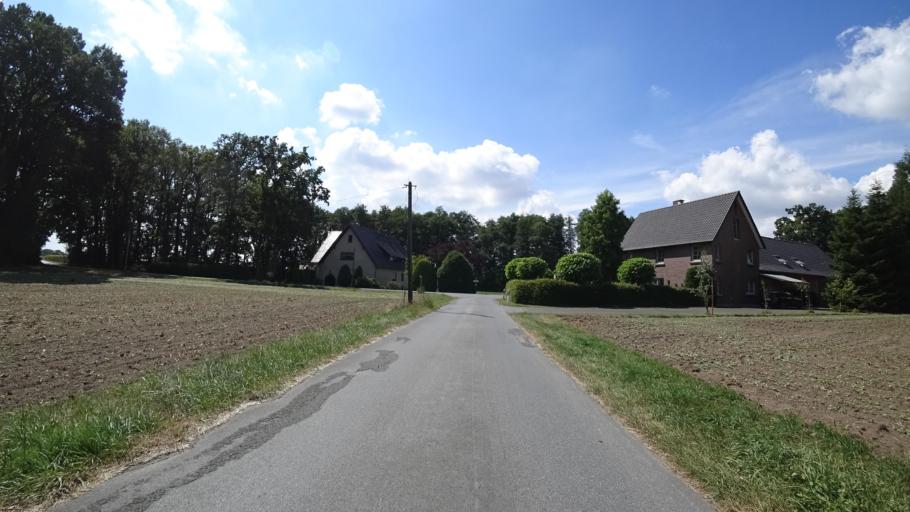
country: DE
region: North Rhine-Westphalia
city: Rietberg
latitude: 51.8678
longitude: 8.4485
